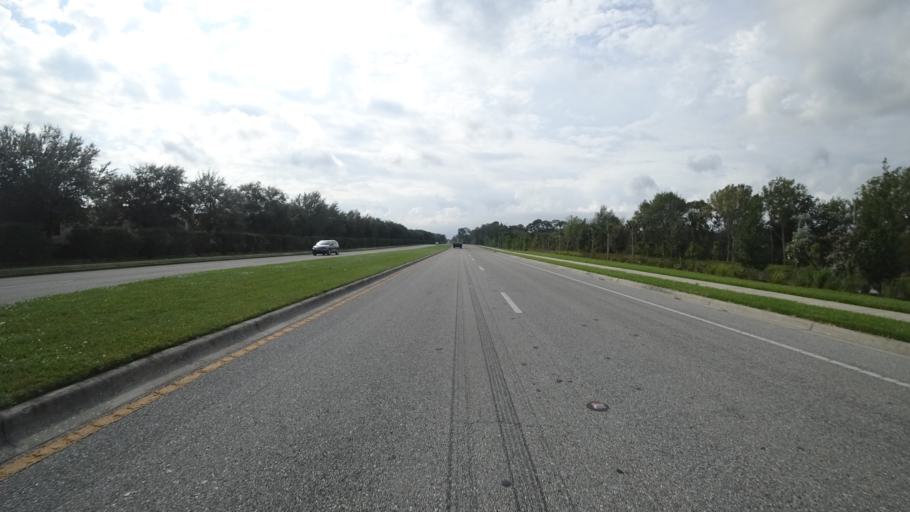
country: US
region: Florida
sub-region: Manatee County
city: Samoset
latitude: 27.4291
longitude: -82.5089
